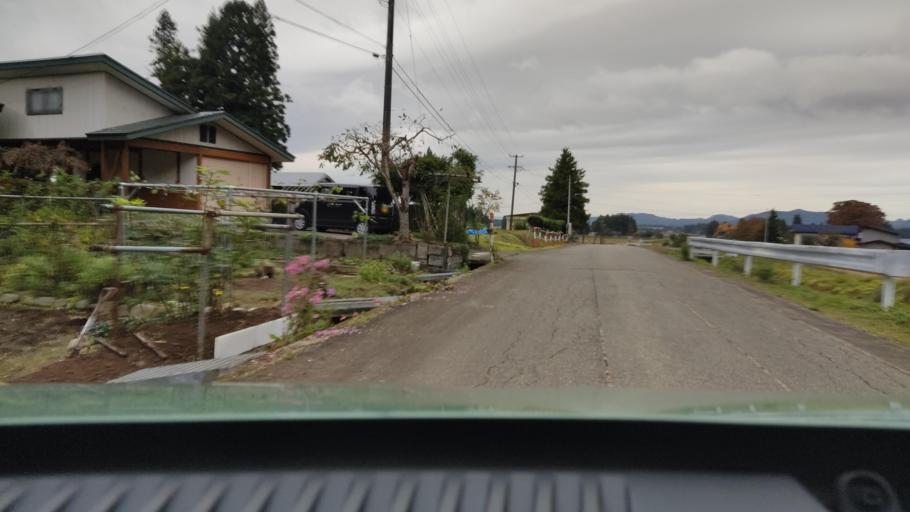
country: JP
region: Akita
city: Kakunodatemachi
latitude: 39.5512
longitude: 140.6240
